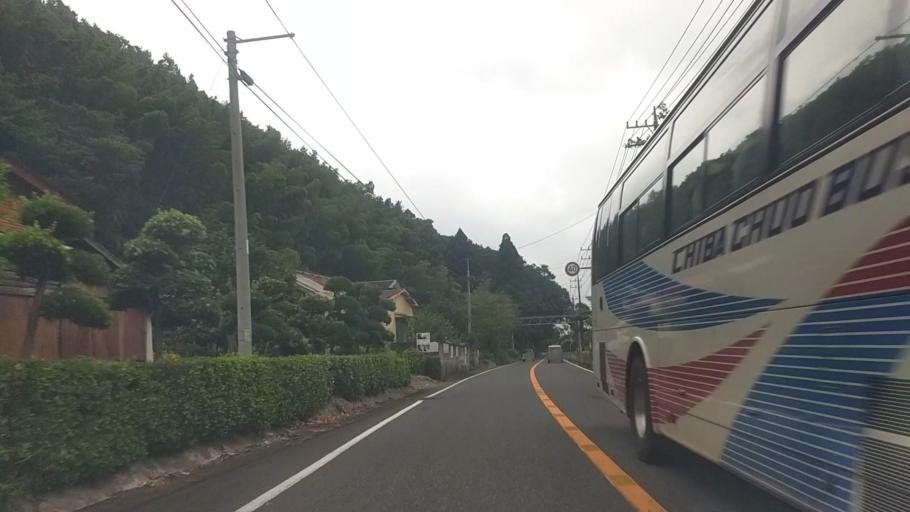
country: JP
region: Chiba
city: Kisarazu
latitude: 35.3043
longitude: 140.0718
